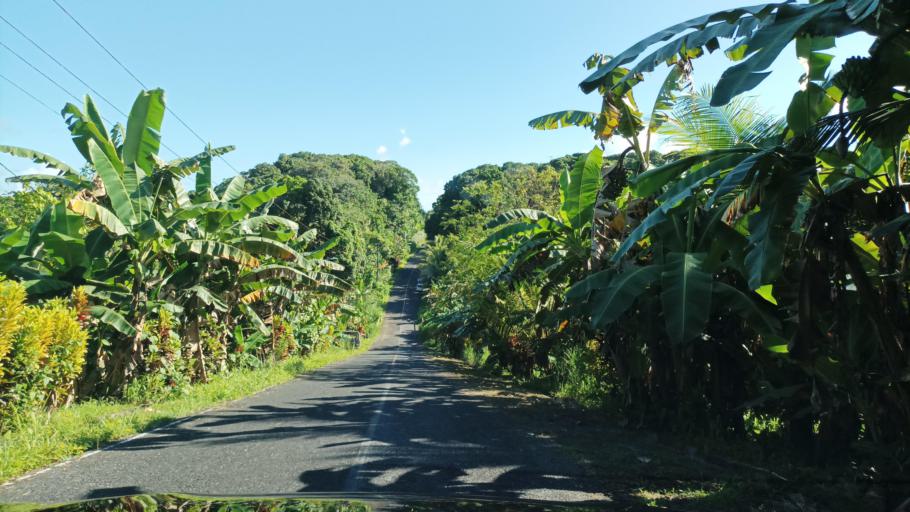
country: FM
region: Pohnpei
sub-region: Madolenihm Municipality
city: Madolenihm Municipality Government
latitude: 6.8154
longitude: 158.2952
